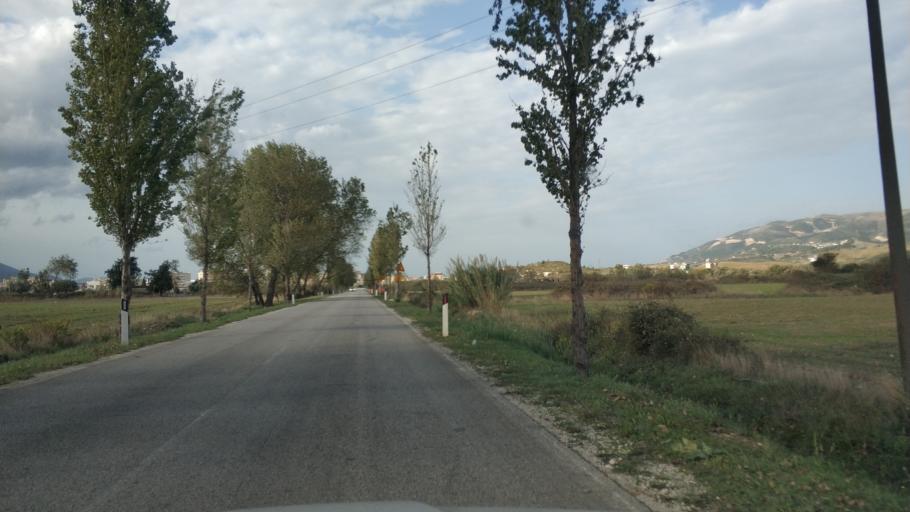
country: AL
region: Vlore
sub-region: Rrethi i Vlores
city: Orikum
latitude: 40.3216
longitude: 19.4815
